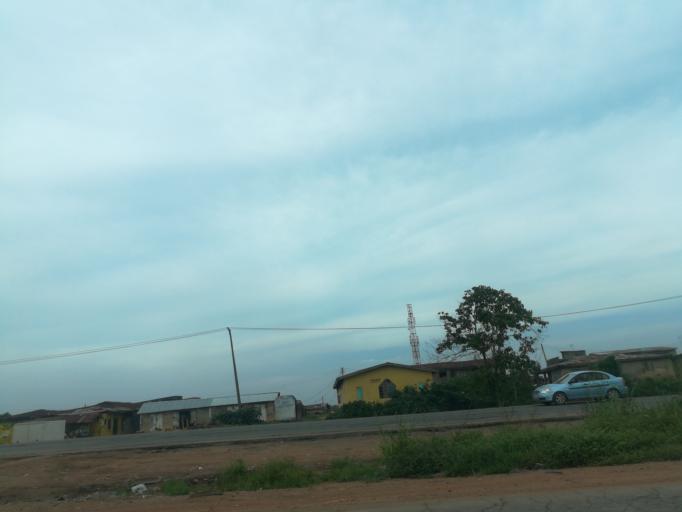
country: NG
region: Oyo
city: Ibadan
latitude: 7.3784
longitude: 3.9300
